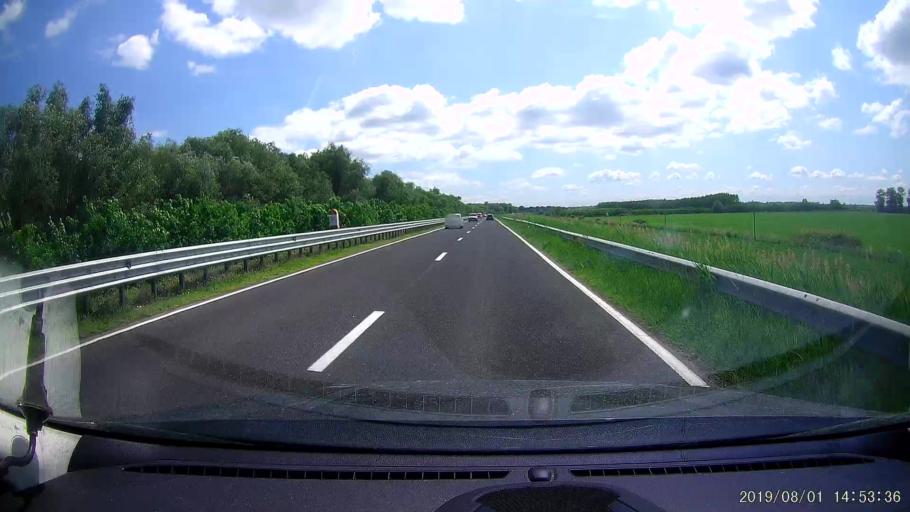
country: RO
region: Braila
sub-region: Municipiul Braila
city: Braila
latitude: 45.3320
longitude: 28.0010
